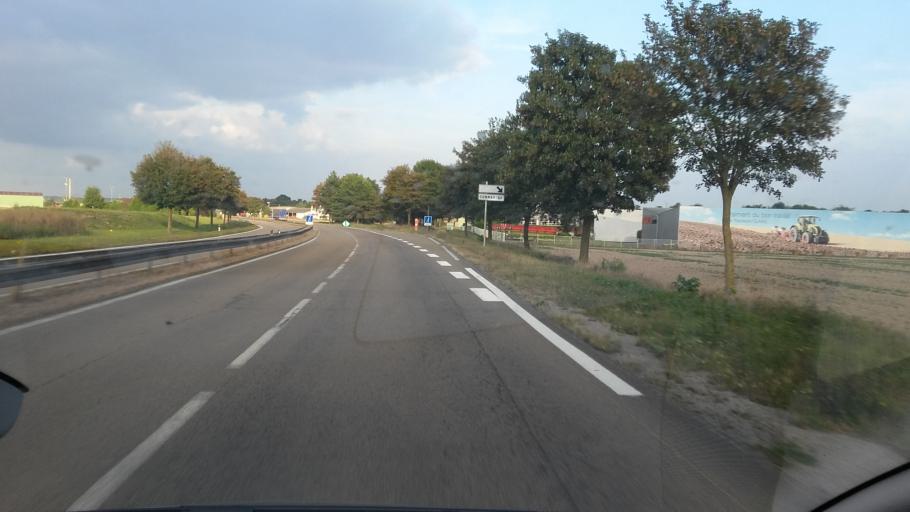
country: FR
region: Champagne-Ardenne
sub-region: Departement de la Marne
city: Connantre
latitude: 48.7307
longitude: 3.9143
